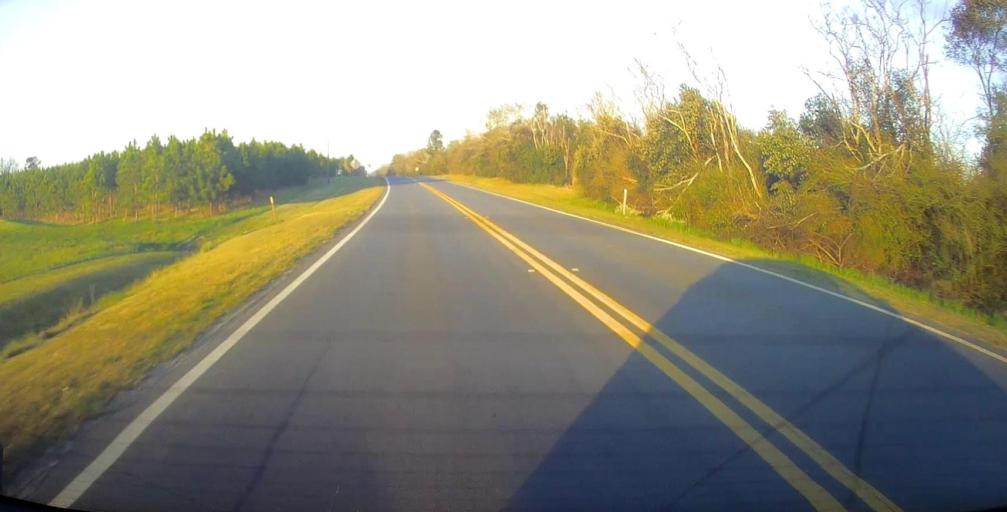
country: US
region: Georgia
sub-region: Dodge County
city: Chester
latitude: 32.3899
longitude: -82.9850
